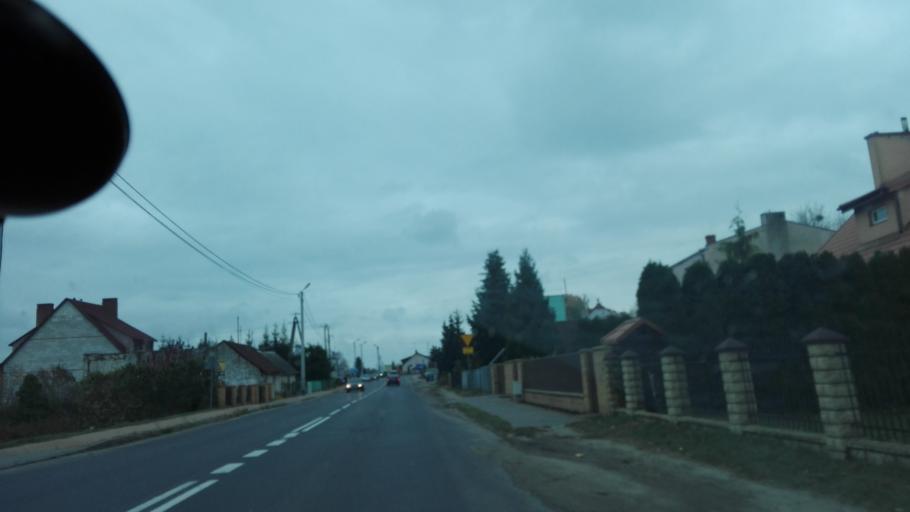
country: PL
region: Lublin Voivodeship
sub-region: Powiat pulawski
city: Pulawy
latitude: 51.4119
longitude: 21.9321
